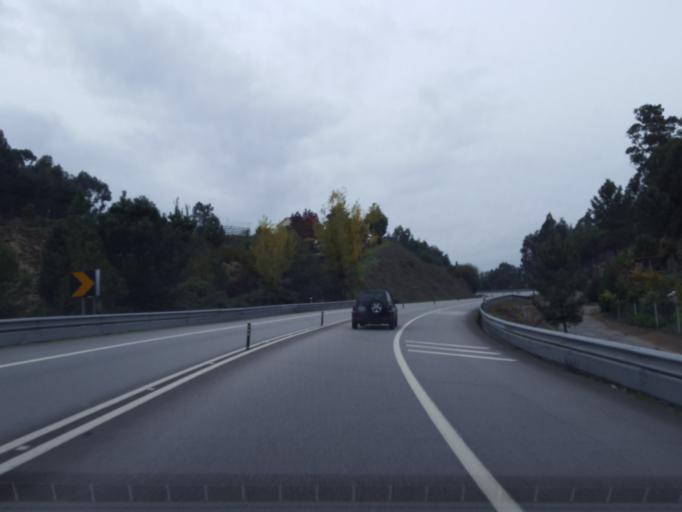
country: PT
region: Porto
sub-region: Marco de Canaveses
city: Marco de Canavezes
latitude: 41.2190
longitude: -8.1851
